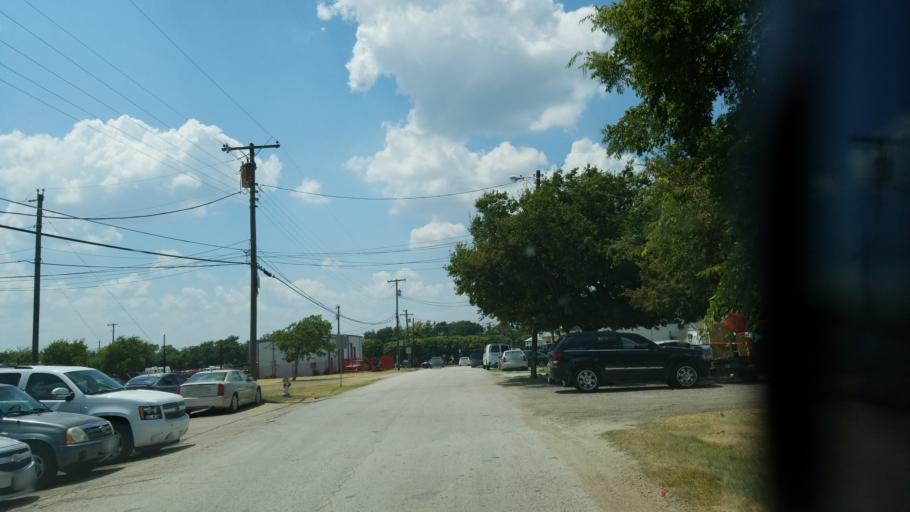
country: US
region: Texas
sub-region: Dallas County
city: Duncanville
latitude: 32.6742
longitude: -96.9025
